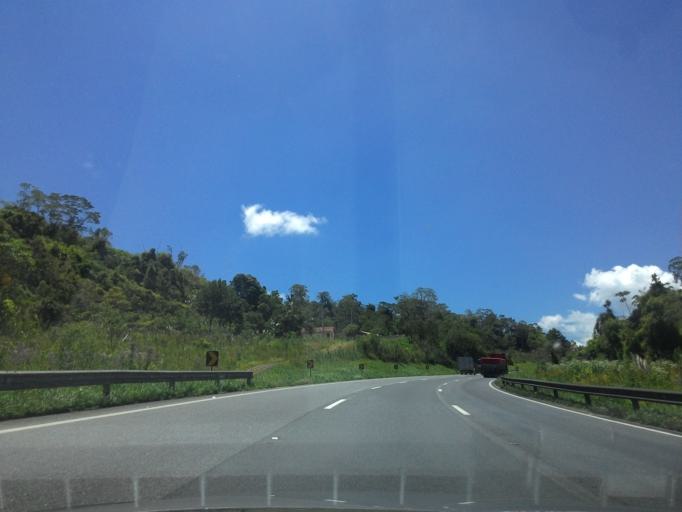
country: BR
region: Parana
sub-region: Antonina
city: Antonina
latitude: -25.0493
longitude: -48.5485
